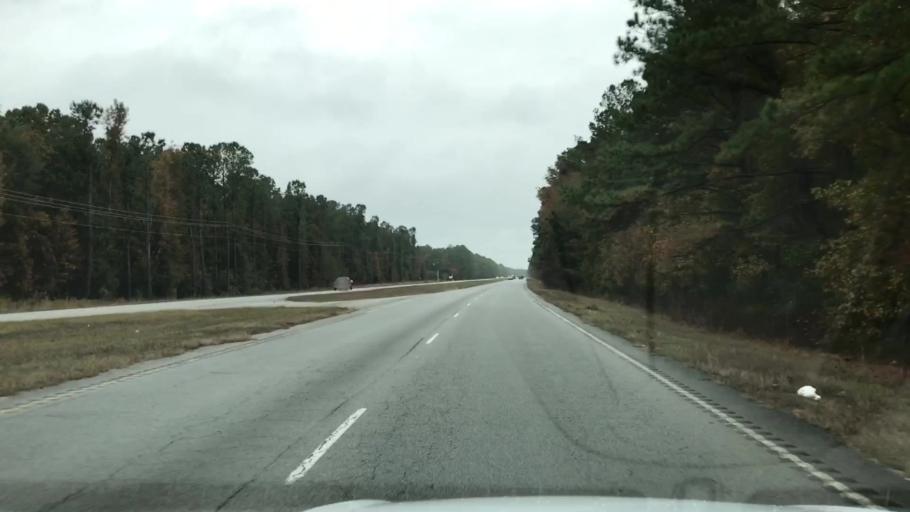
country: US
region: South Carolina
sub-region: Charleston County
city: Awendaw
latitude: 32.9570
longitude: -79.6912
